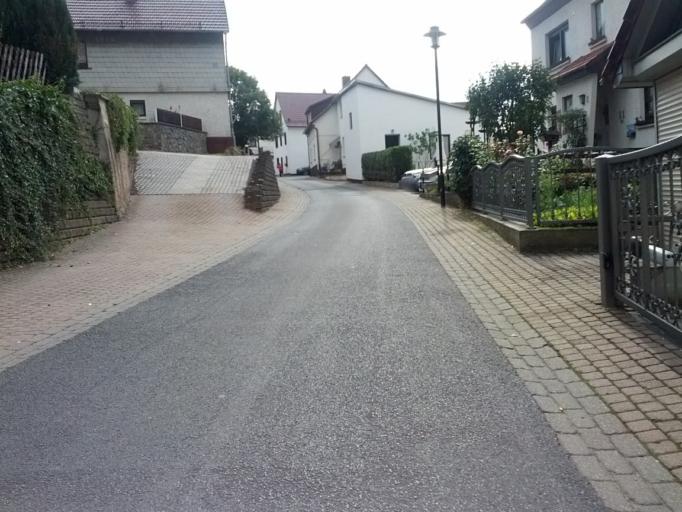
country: DE
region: Thuringia
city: Thal
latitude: 50.9409
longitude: 10.3930
